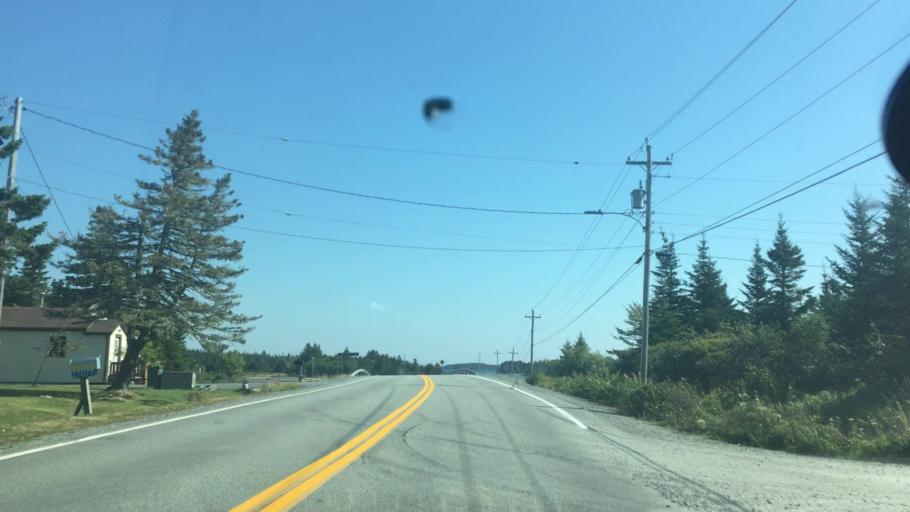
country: CA
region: Nova Scotia
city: New Glasgow
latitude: 44.9170
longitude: -62.3097
